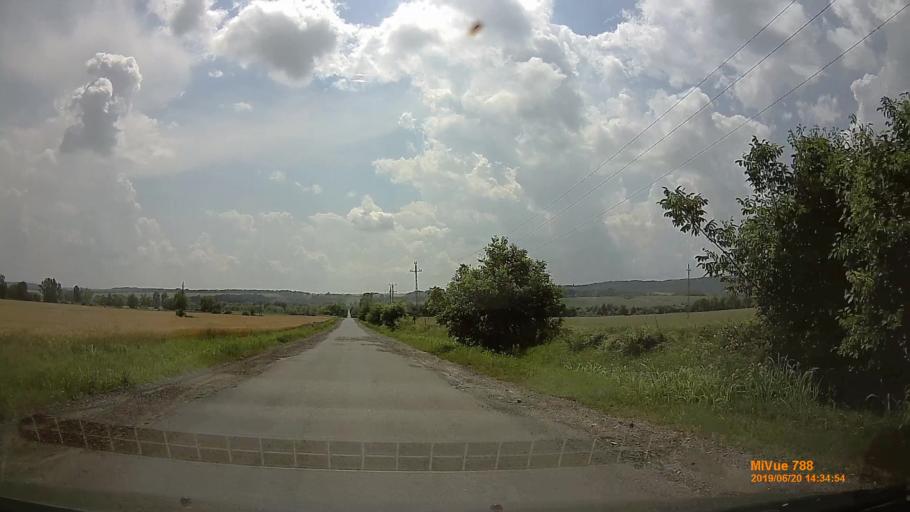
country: HU
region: Baranya
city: Hosszuheteny
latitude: 46.1155
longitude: 18.3309
